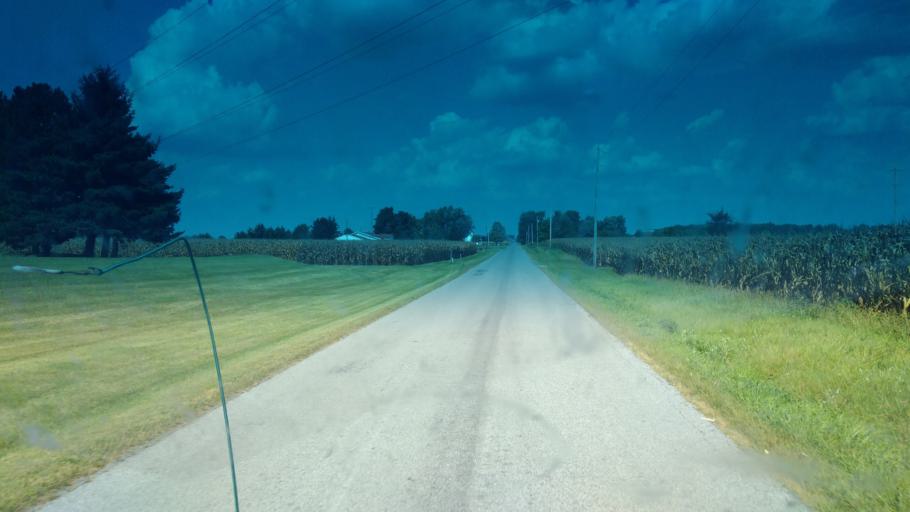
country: US
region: Ohio
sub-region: Hardin County
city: Ada
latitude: 40.6910
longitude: -83.8800
